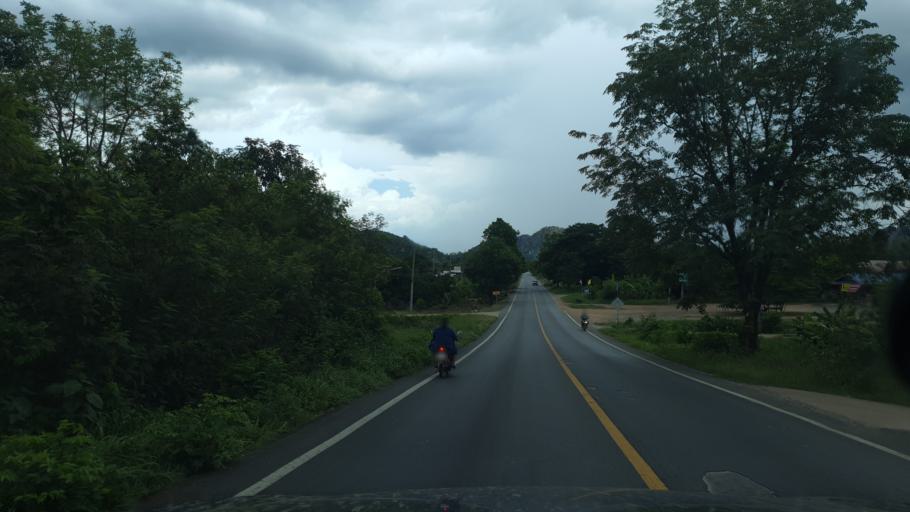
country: TH
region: Sukhothai
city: Thung Saliam
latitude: 17.3358
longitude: 99.4781
